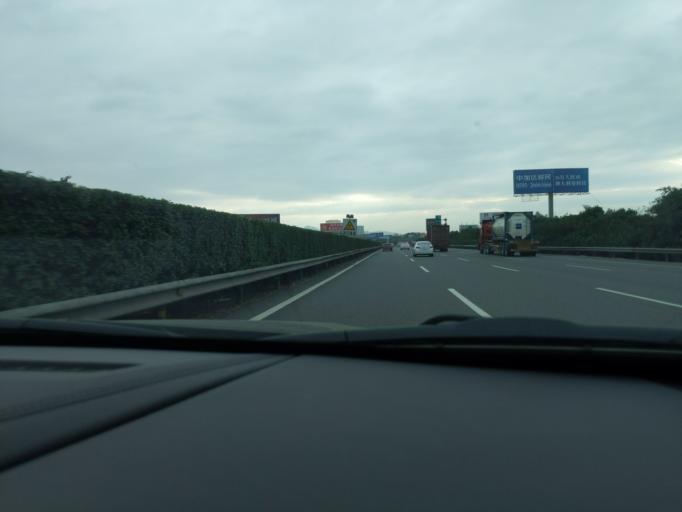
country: CN
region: Fujian
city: Anhai
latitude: 24.7397
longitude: 118.4242
